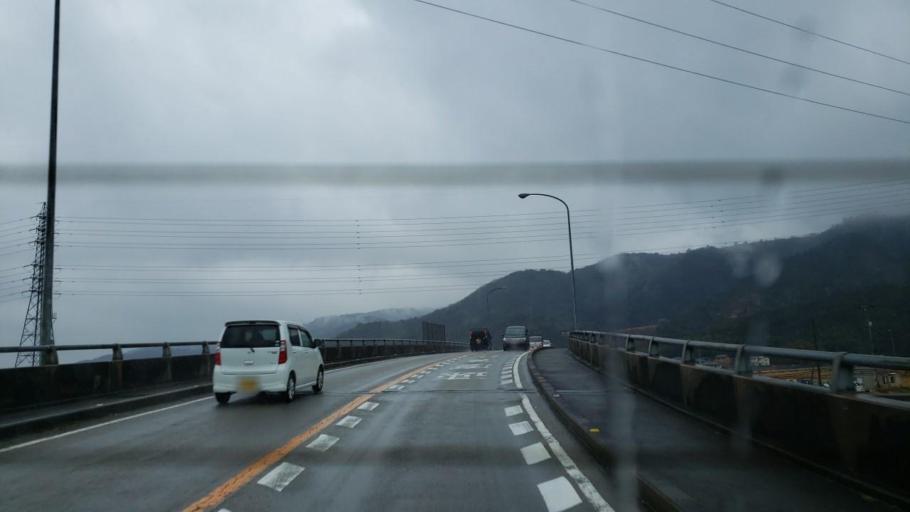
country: JP
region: Tokushima
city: Narutocho-mitsuishi
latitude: 34.1608
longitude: 134.5553
